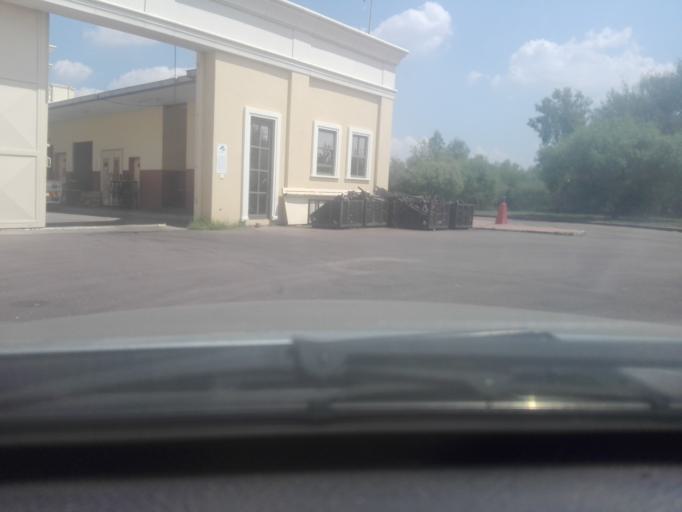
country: BW
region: Kweneng
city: Mogoditshane
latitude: -24.6400
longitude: 25.8757
